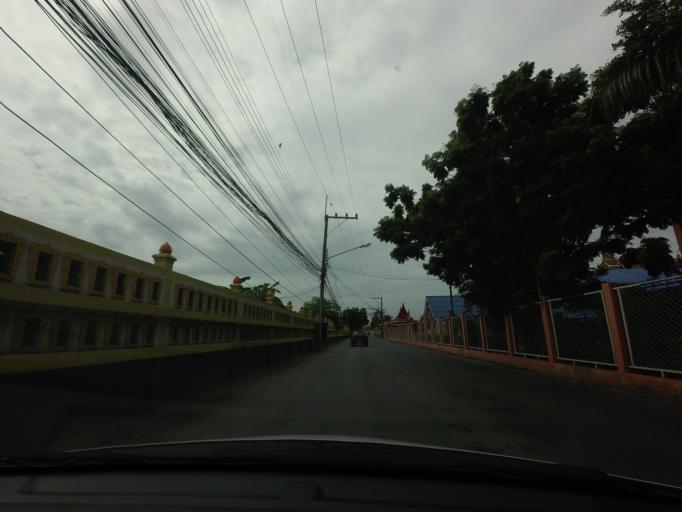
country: TH
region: Pathum Thani
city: Lam Luk Ka
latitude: 13.9297
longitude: 100.7132
